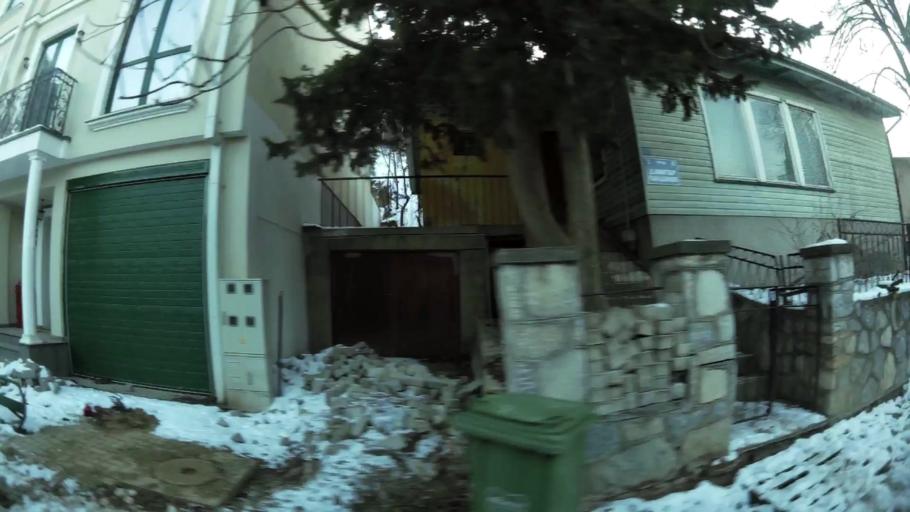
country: MK
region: Karpos
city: Skopje
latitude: 41.9907
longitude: 21.4097
